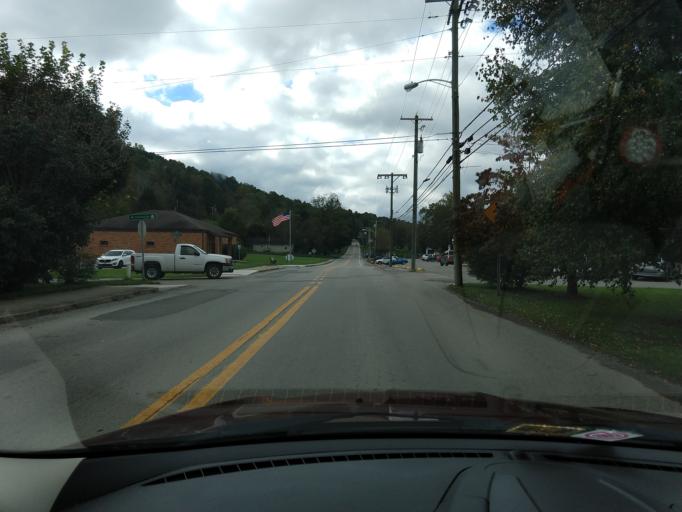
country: US
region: West Virginia
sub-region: Barbour County
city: Belington
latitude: 39.0227
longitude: -79.9369
